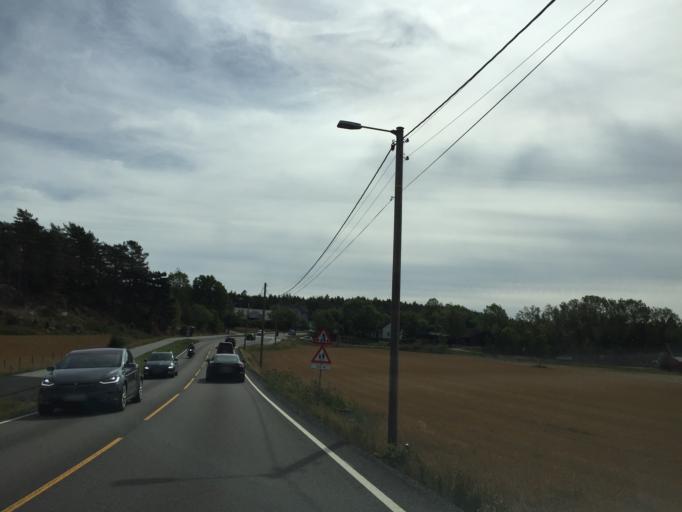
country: NO
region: Ostfold
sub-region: Fredrikstad
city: Fredrikstad
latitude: 59.1619
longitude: 10.9290
